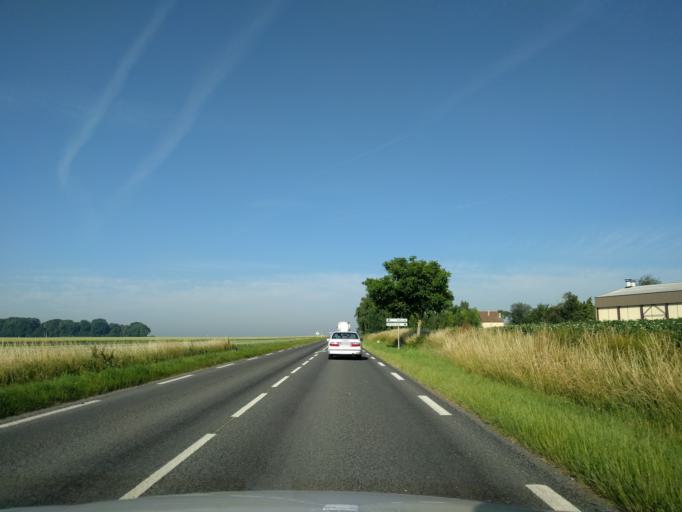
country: FR
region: Picardie
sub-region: Departement de la Somme
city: Roye
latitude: 49.6588
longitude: 2.7105
